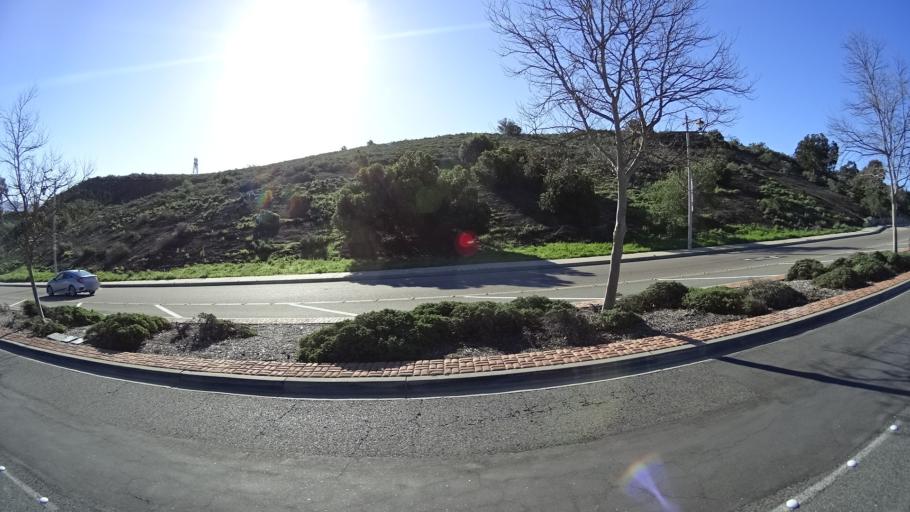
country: US
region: California
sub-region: Orange County
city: Villa Park
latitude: 33.8364
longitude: -117.7945
